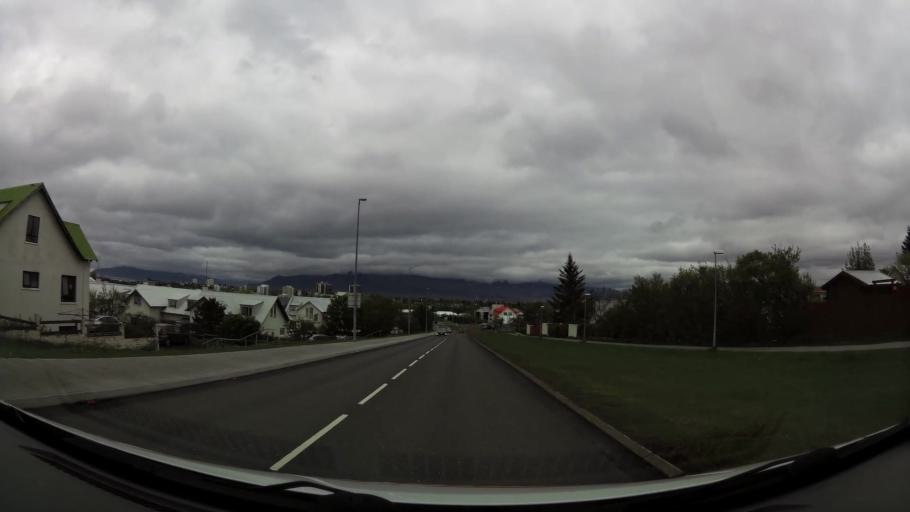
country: IS
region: Capital Region
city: Reykjavik
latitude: 64.1242
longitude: -21.8663
